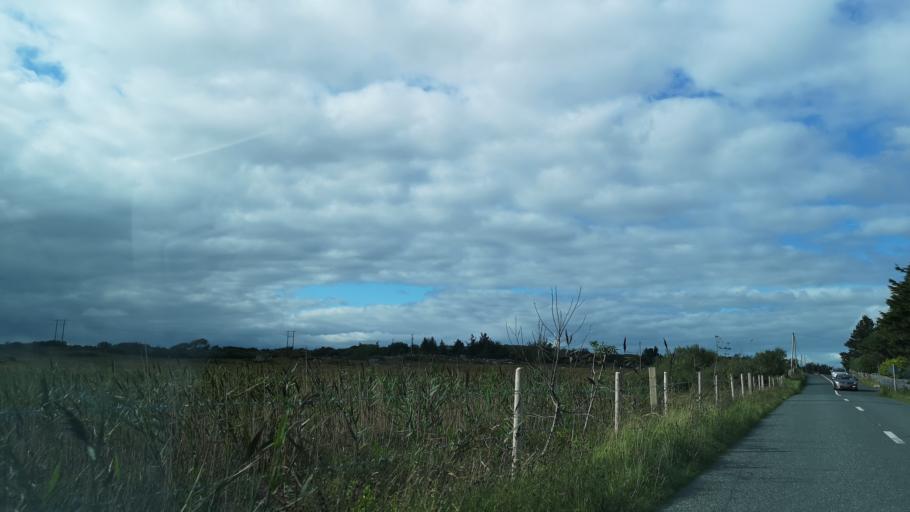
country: IE
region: Connaught
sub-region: County Galway
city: Bearna
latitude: 53.2883
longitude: -9.1635
